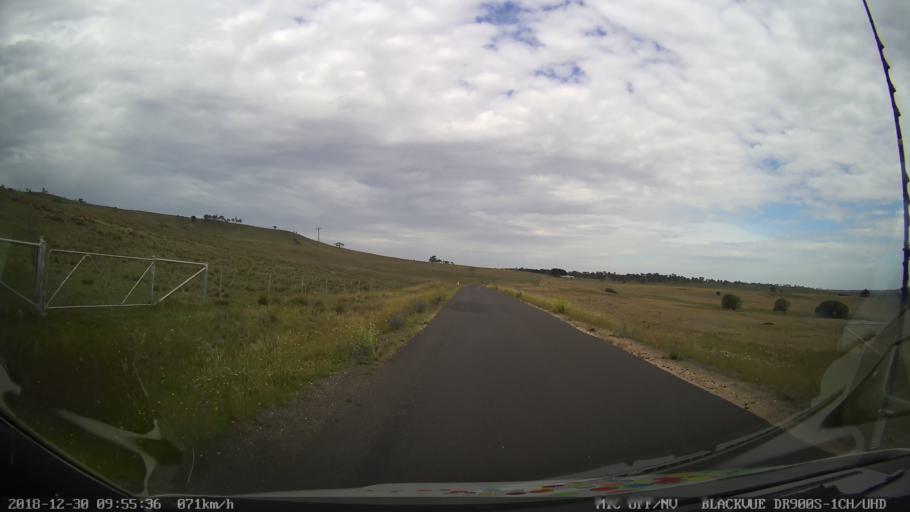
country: AU
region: New South Wales
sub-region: Cooma-Monaro
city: Cooma
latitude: -36.5213
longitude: 149.2626
